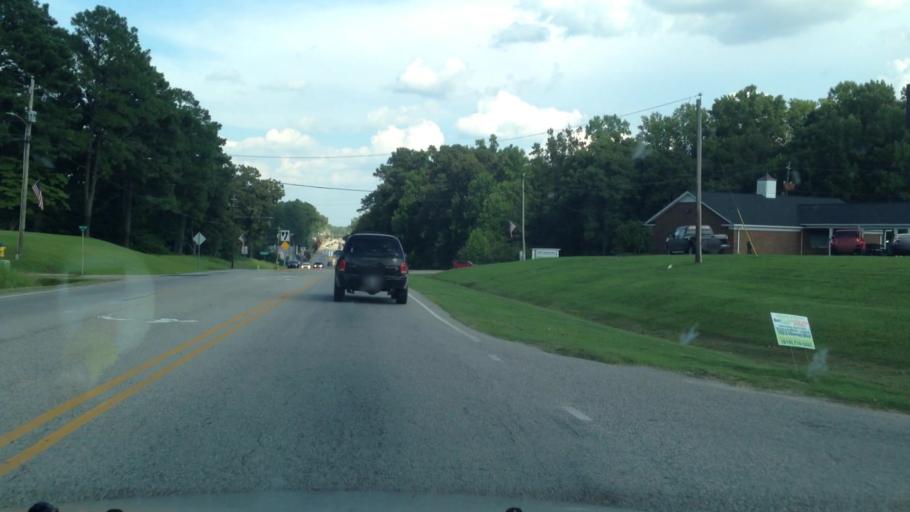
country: US
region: North Carolina
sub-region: Harnett County
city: Lillington
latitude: 35.4018
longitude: -78.8278
